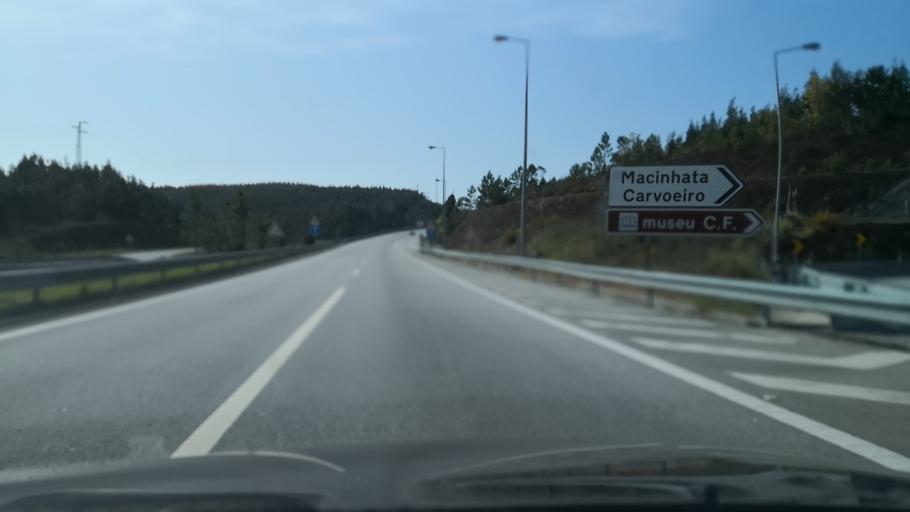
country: PT
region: Aveiro
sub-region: Albergaria-A-Velha
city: Albergaria-a-Velha
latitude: 40.6783
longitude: -8.4421
